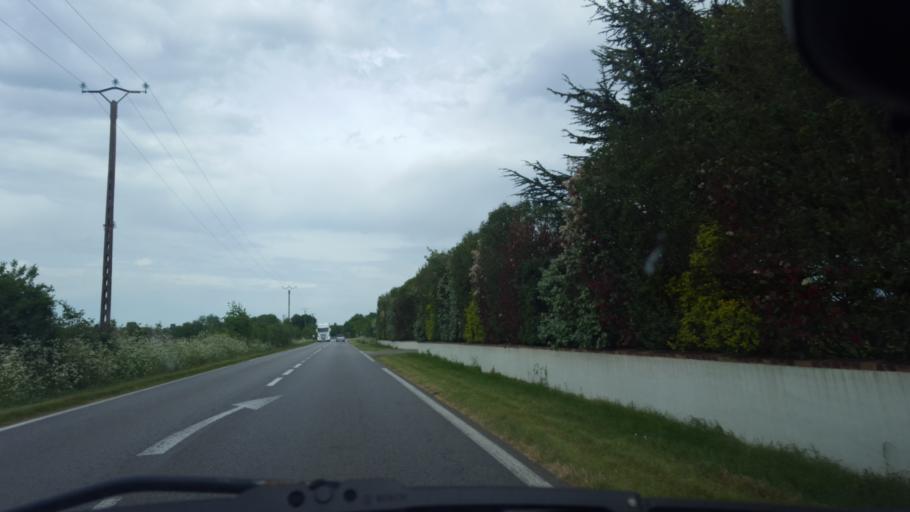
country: FR
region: Pays de la Loire
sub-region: Departement de la Loire-Atlantique
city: Paulx
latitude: 46.9935
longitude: -1.7590
